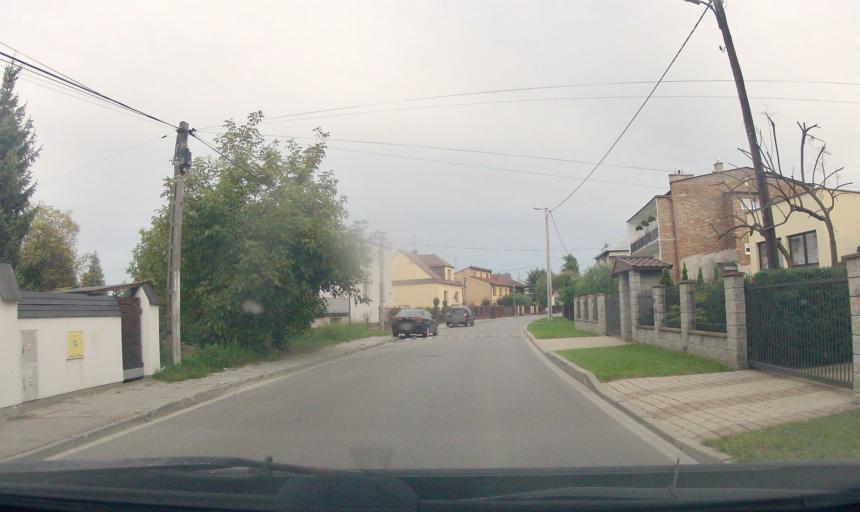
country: PL
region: Lesser Poland Voivodeship
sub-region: Krakow
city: Krakow
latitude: 50.0392
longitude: 19.9886
